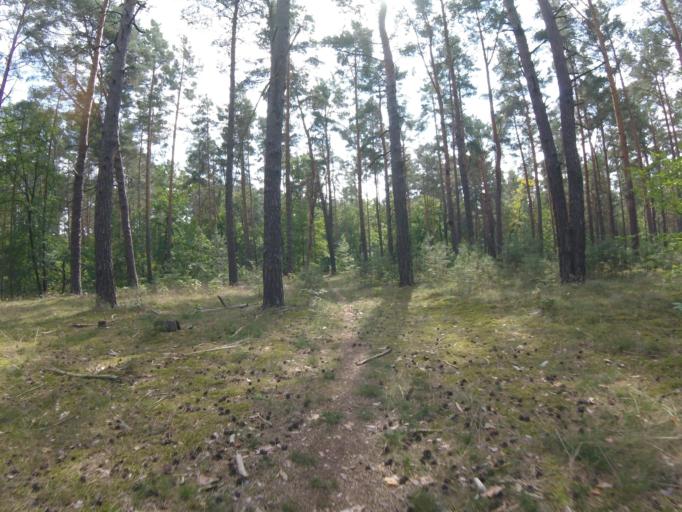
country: DE
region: Brandenburg
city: Konigs Wusterhausen
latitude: 52.2845
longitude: 13.6675
